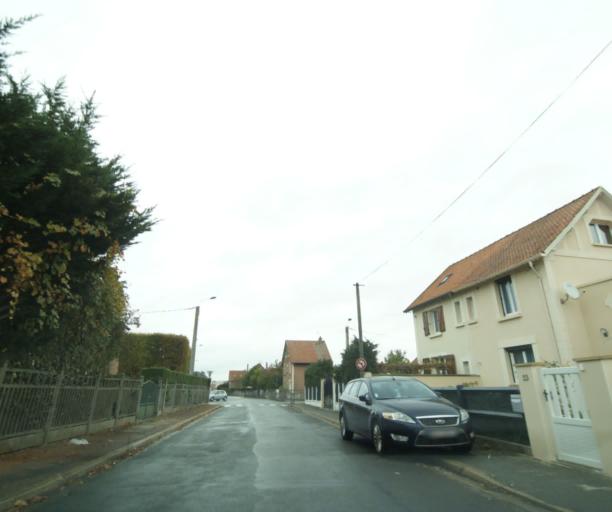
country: FR
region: Centre
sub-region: Departement d'Eure-et-Loir
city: Vernouillet
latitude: 48.7245
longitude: 1.3792
